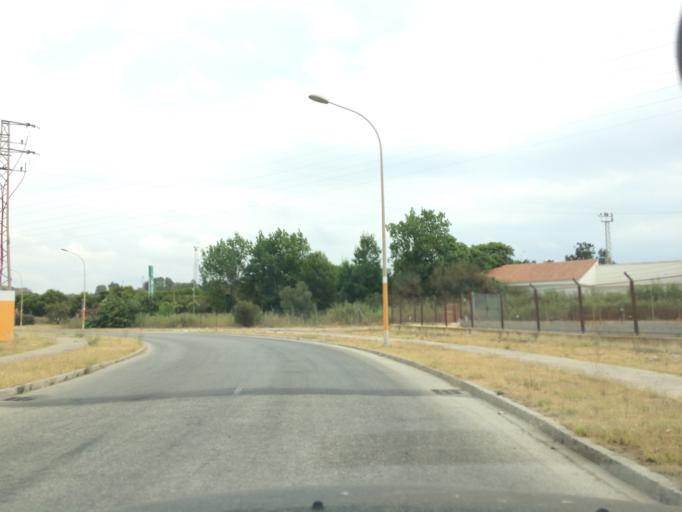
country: ES
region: Andalusia
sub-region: Provincia de Malaga
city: Malaga
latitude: 36.6957
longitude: -4.4800
